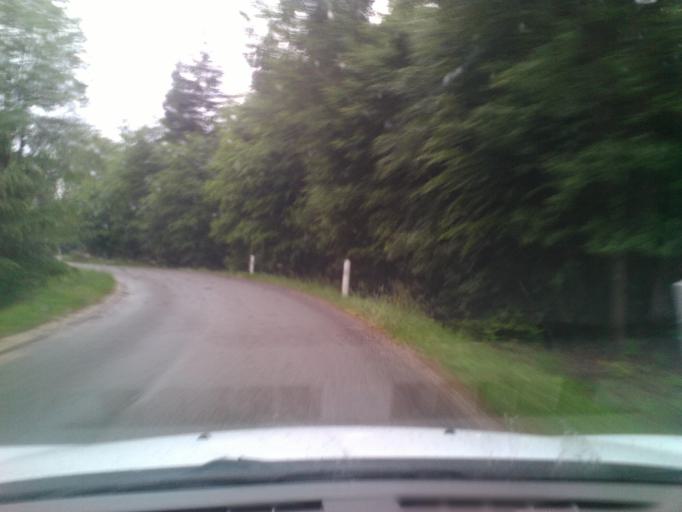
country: FR
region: Lorraine
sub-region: Departement des Vosges
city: Jeanmenil
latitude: 48.2804
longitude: 6.7071
